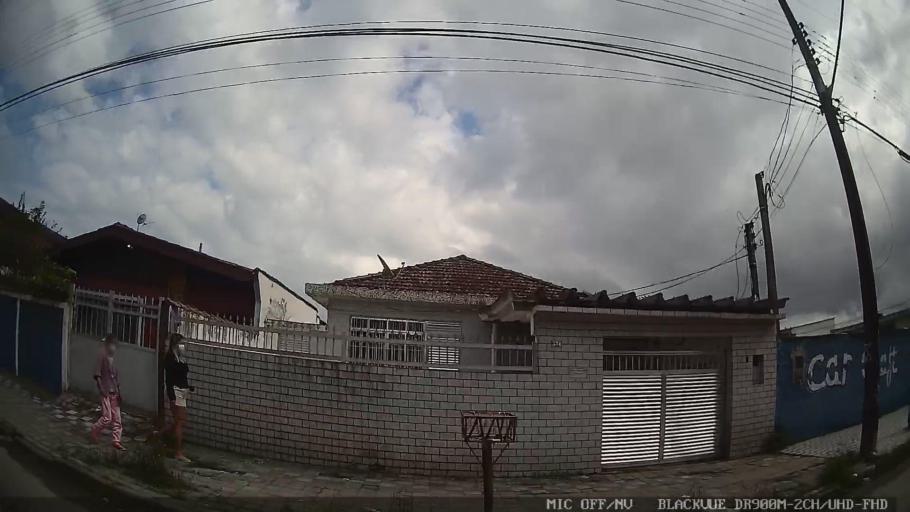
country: BR
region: Sao Paulo
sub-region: Guaruja
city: Guaruja
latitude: -23.9959
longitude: -46.2815
